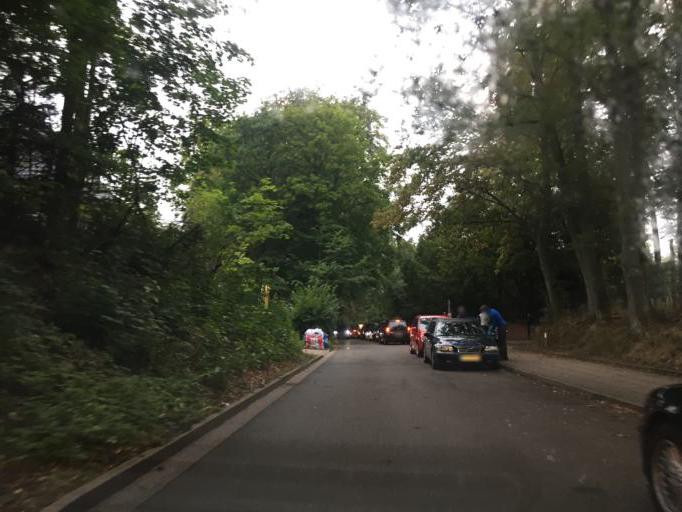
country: DE
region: Hamburg
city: Hummelsbuettel
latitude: 53.6322
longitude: 10.0469
